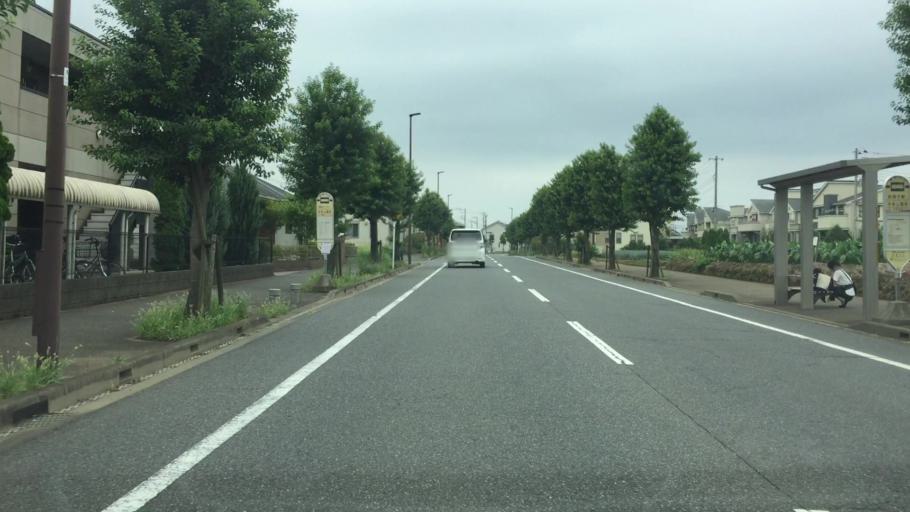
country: JP
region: Chiba
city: Abiko
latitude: 35.8470
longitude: 140.0255
